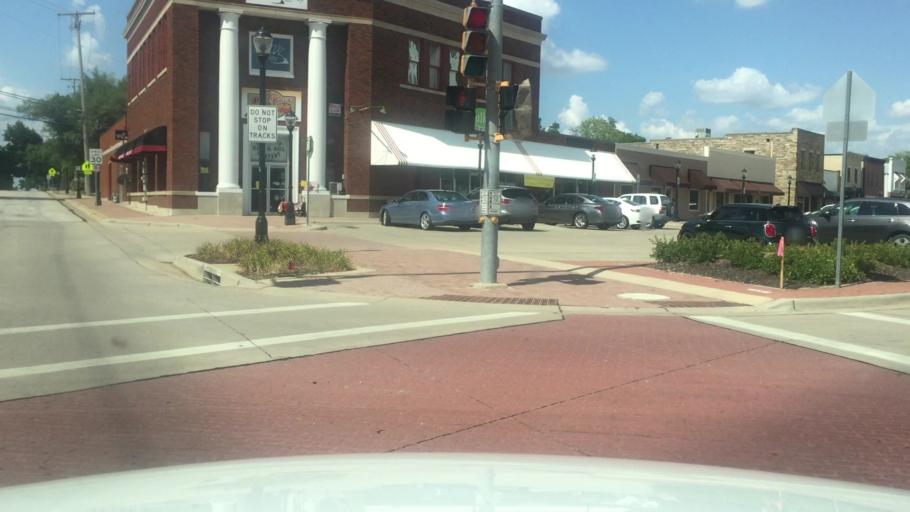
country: US
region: Kansas
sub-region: Johnson County
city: Lenexa
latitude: 38.9603
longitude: -94.7422
